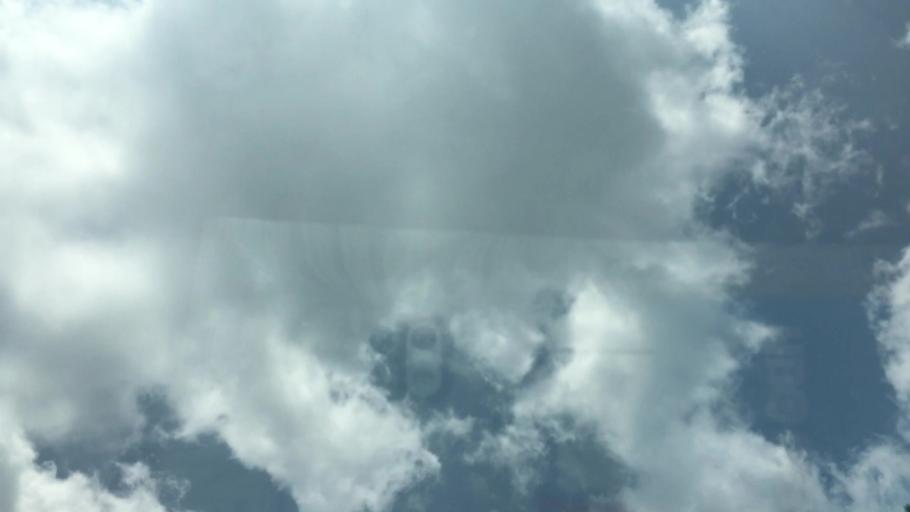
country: US
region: Alabama
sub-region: Pickens County
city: Gordo
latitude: 33.2820
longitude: -87.8096
